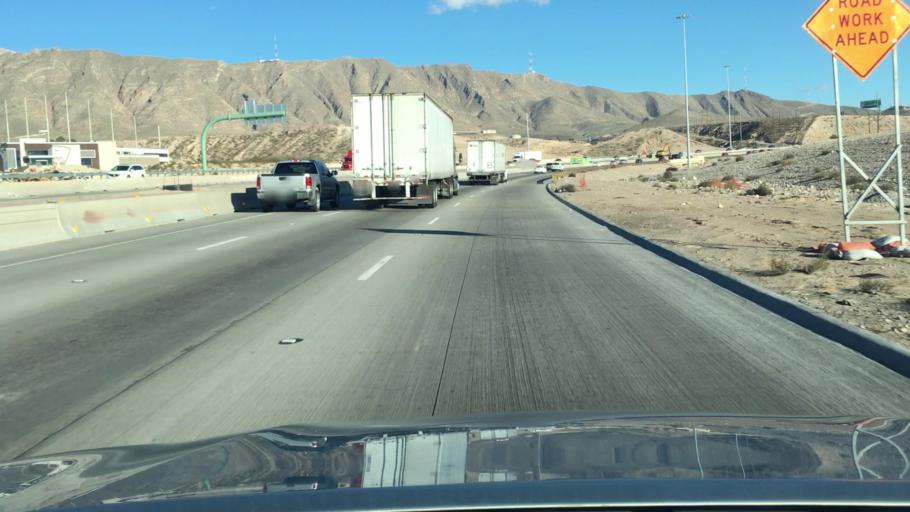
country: US
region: New Mexico
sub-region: Dona Ana County
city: Sunland Park
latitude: 31.8092
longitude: -106.5289
